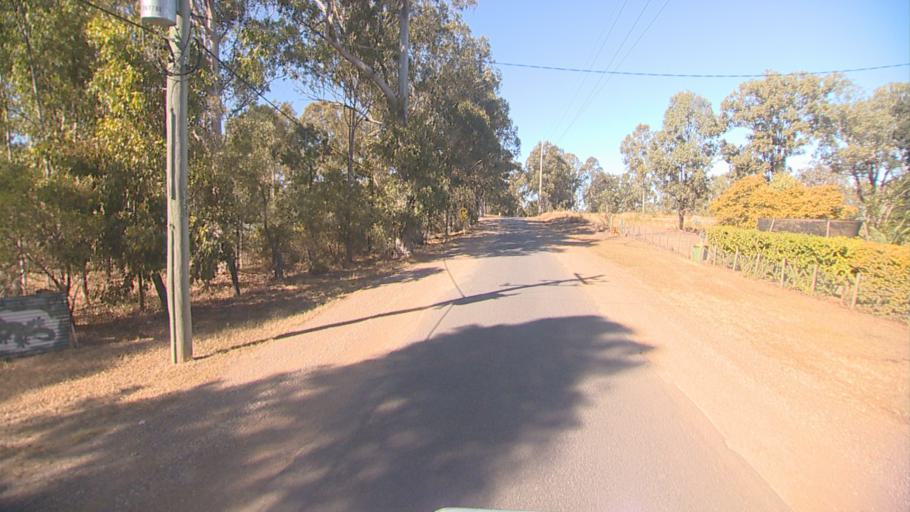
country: AU
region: Queensland
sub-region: Logan
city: Cedar Vale
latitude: -27.8909
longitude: 153.0175
